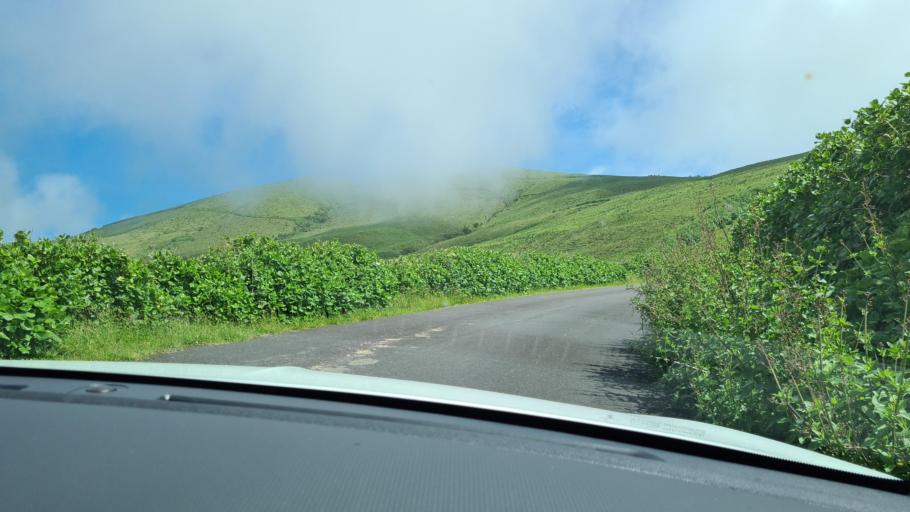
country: PT
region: Azores
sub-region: Sao Roque do Pico
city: Sao Roque do Pico
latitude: 38.6712
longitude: -28.1335
